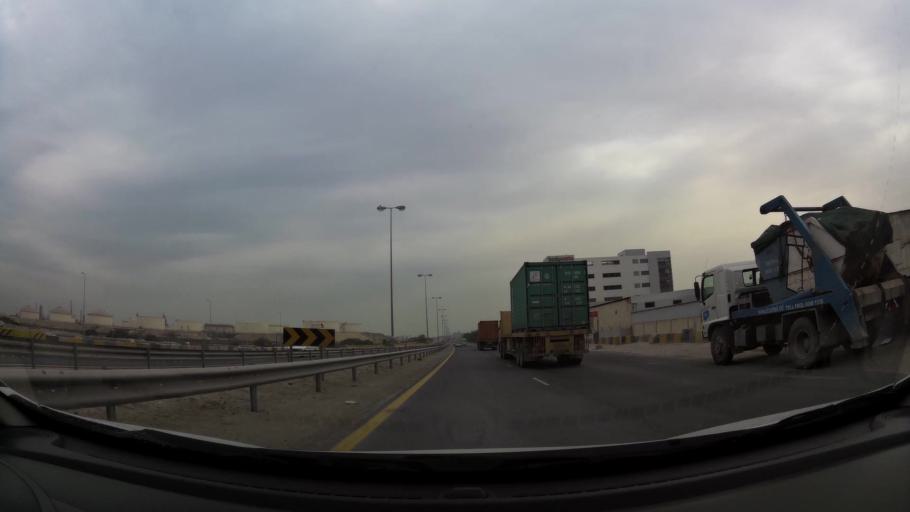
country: BH
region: Northern
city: Ar Rifa'
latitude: 26.1186
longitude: 50.5930
